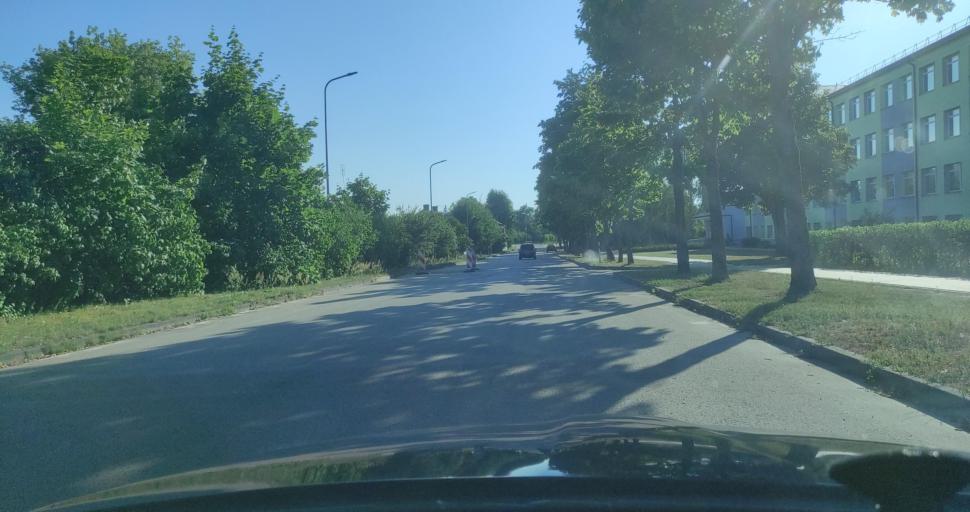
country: LV
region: Skrunda
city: Skrunda
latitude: 56.6746
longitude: 22.0120
